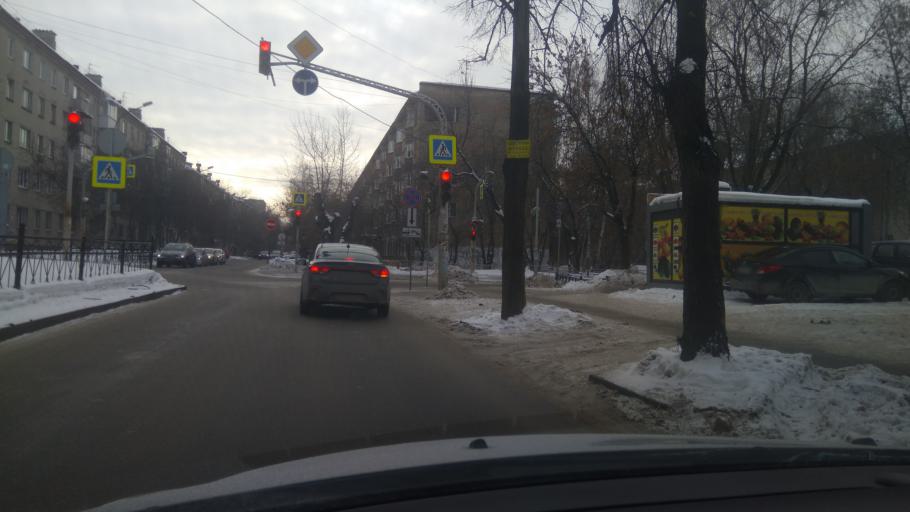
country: RU
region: Sverdlovsk
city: Yekaterinburg
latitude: 56.8461
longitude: 60.6237
